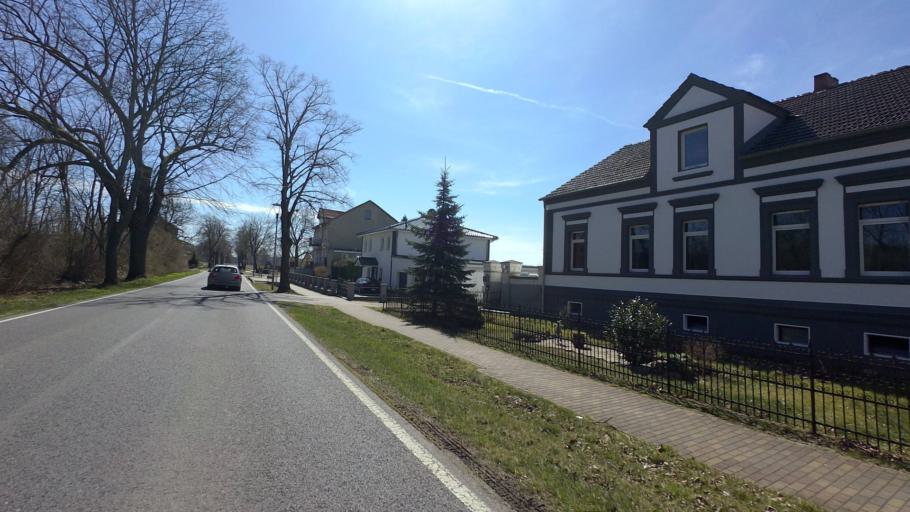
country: DE
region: Brandenburg
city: Mittenwalde
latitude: 52.2361
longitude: 13.5676
